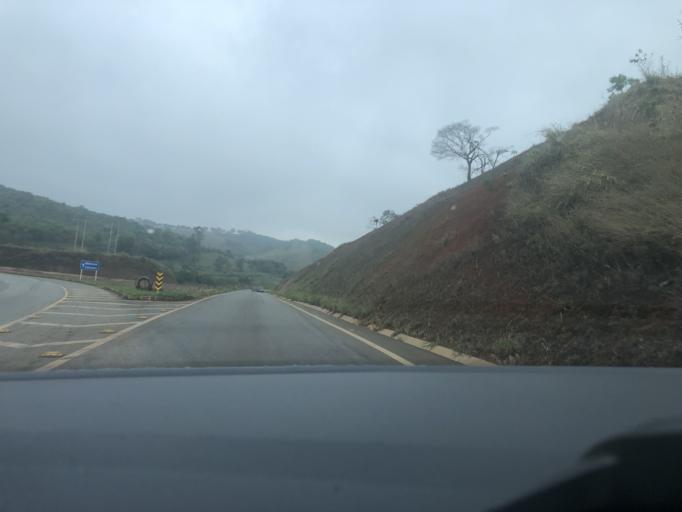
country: BR
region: Minas Gerais
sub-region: Congonhas
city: Congonhas
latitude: -20.6026
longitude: -43.9335
